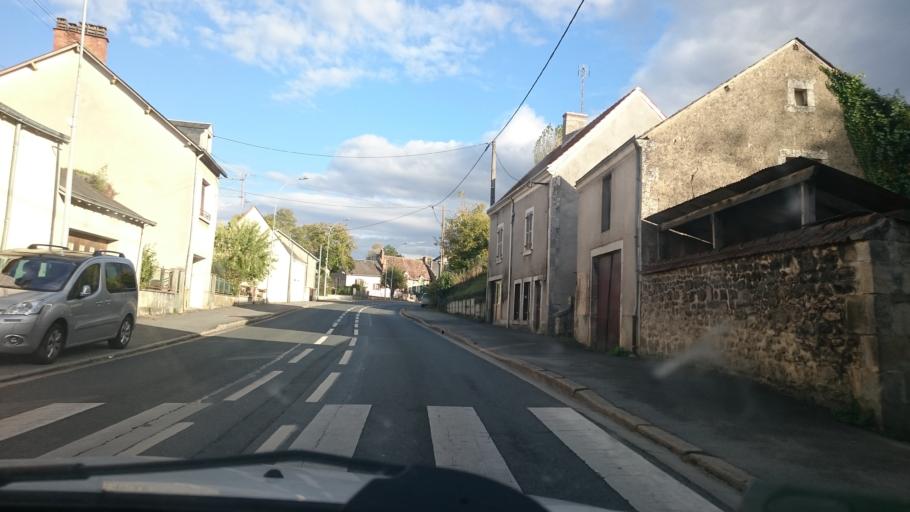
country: FR
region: Centre
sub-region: Departement de l'Indre
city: Saint-Marcel
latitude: 46.6284
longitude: 1.4811
